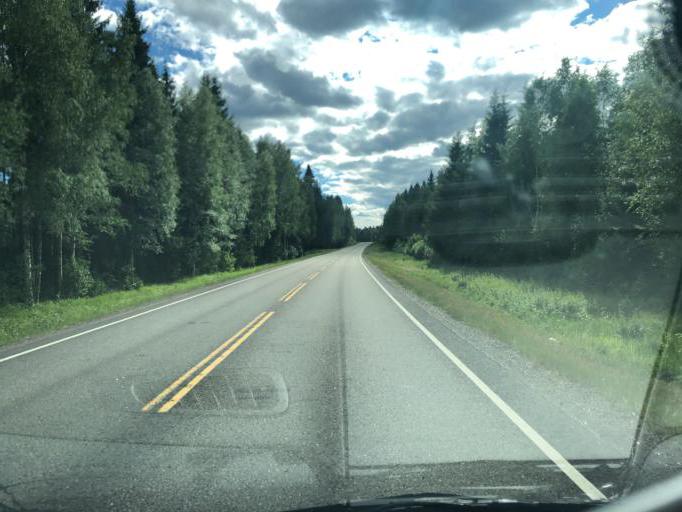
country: FI
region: Kymenlaakso
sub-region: Kouvola
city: Kouvola
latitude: 61.0011
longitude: 26.9373
